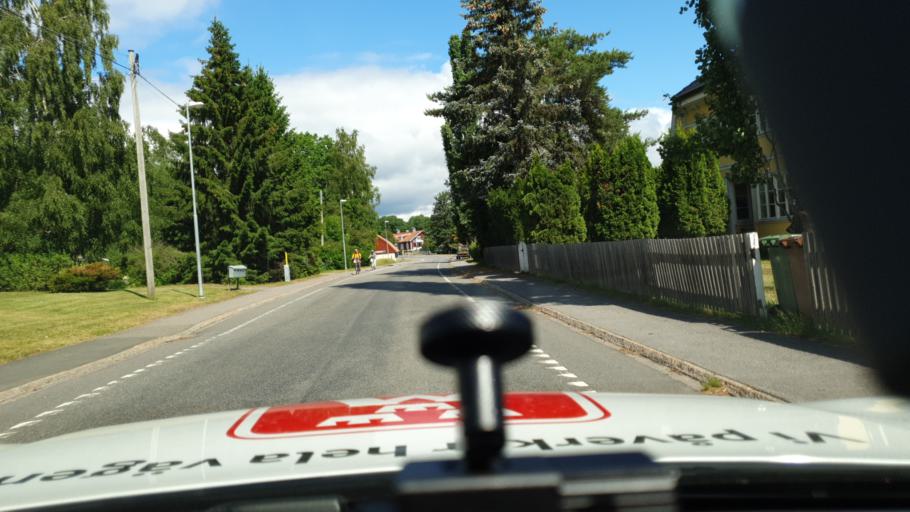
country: SE
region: Vaestra Goetaland
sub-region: Karlsborgs Kommun
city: Karlsborg
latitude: 58.5774
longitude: 14.4350
